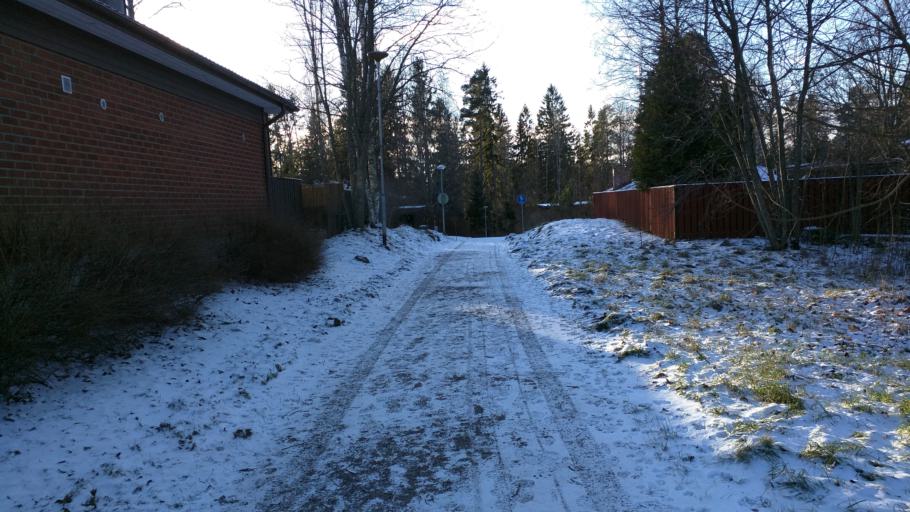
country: FI
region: Uusimaa
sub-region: Helsinki
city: Kilo
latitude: 60.2432
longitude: 24.7645
